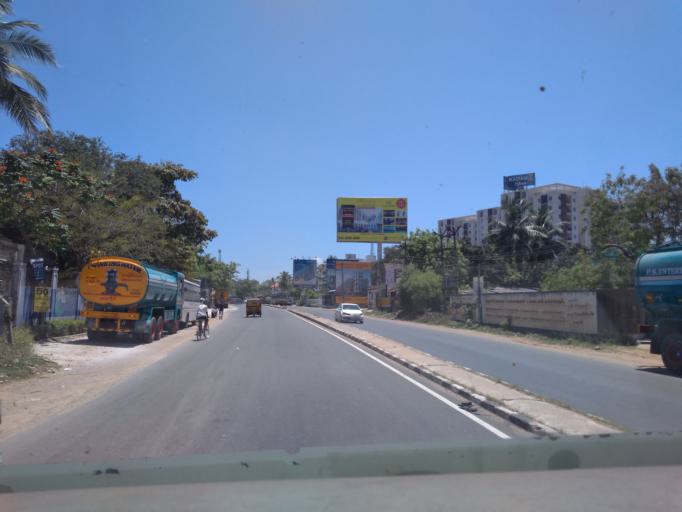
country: IN
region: Tamil Nadu
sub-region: Kancheepuram
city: Injambakkam
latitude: 12.8228
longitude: 80.2308
